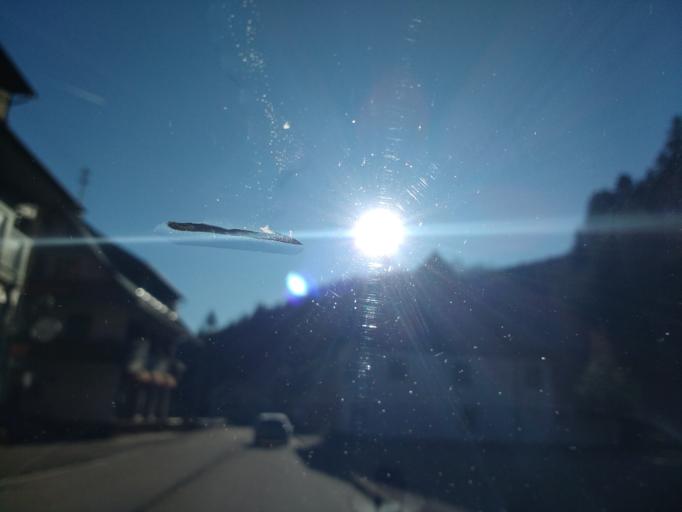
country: DE
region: Baden-Wuerttemberg
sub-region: Karlsruhe Region
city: Bad Rippoldsau-Schapbach
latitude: 48.4387
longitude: 8.3147
